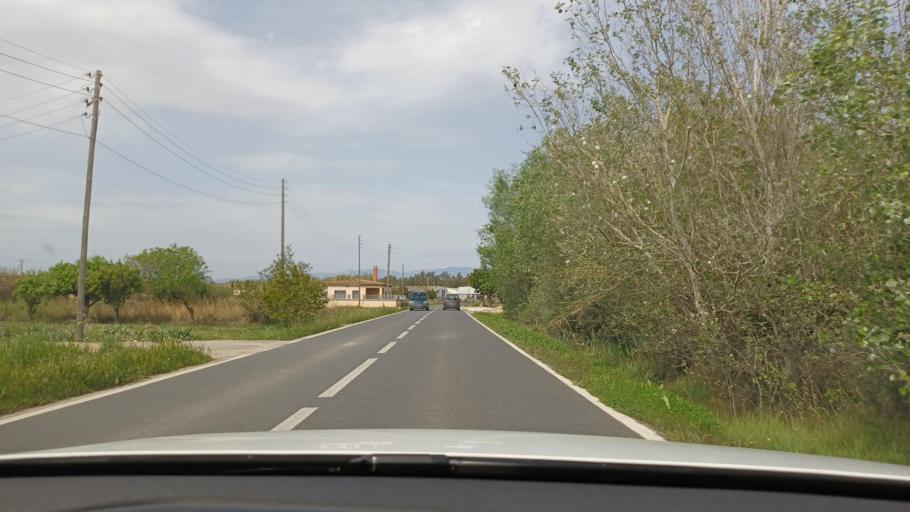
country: ES
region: Catalonia
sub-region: Provincia de Tarragona
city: Amposta
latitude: 40.7062
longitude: 0.5969
